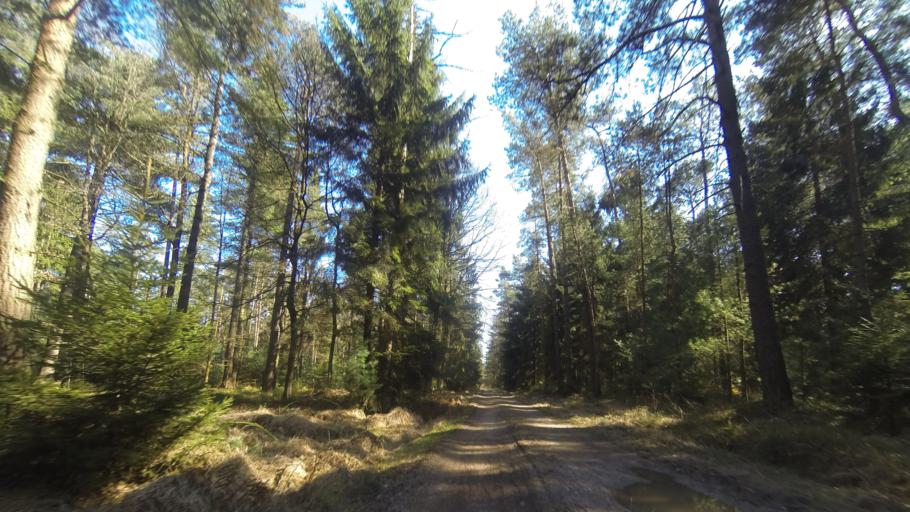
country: DE
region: Saxony
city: Ottendorf-Okrilla
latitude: 51.2151
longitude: 13.7987
